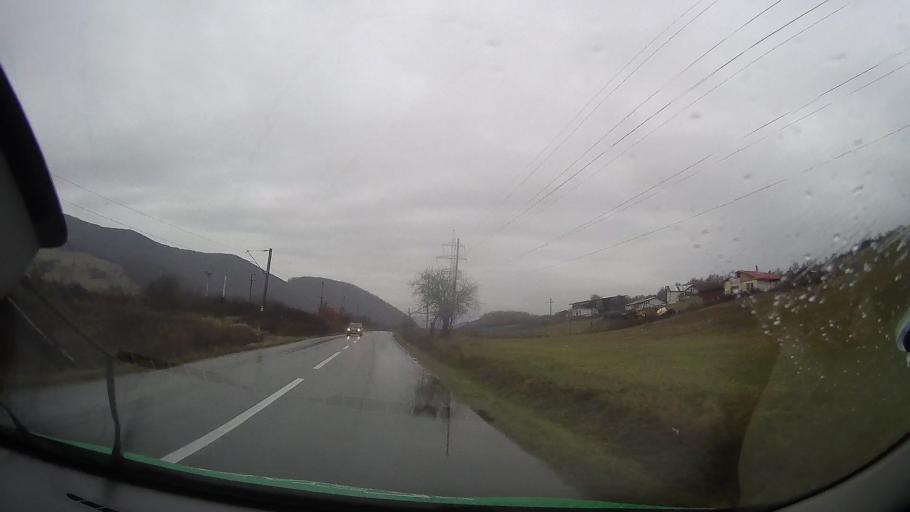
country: RO
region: Bistrita-Nasaud
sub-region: Municipiul Bistrita
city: Viisoara
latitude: 47.0483
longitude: 24.4614
